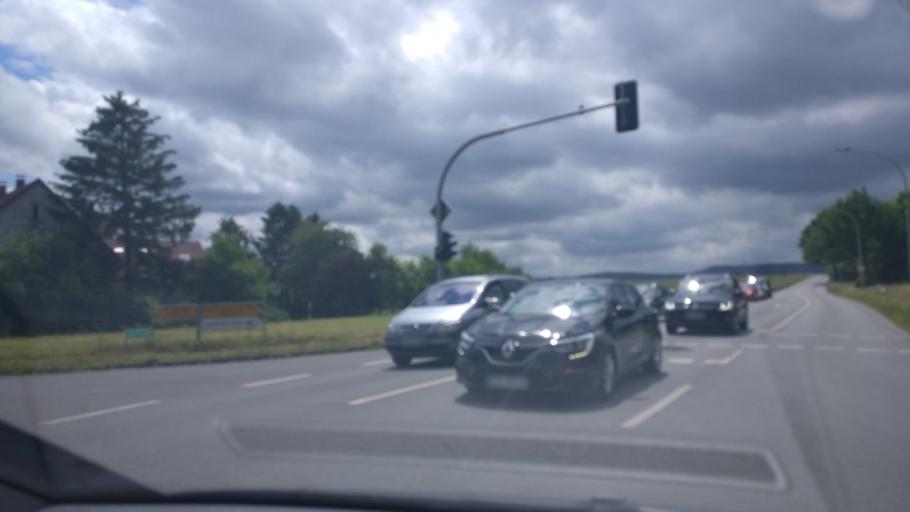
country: DE
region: North Rhine-Westphalia
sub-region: Regierungsbezirk Detmold
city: Leopoldshohe
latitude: 51.9927
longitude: 8.7237
